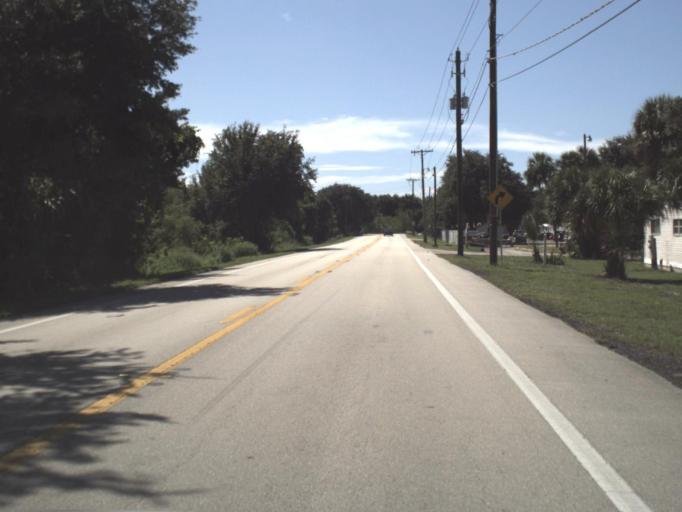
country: US
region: Florida
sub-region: Polk County
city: Polk City
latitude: 28.1384
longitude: -81.7958
